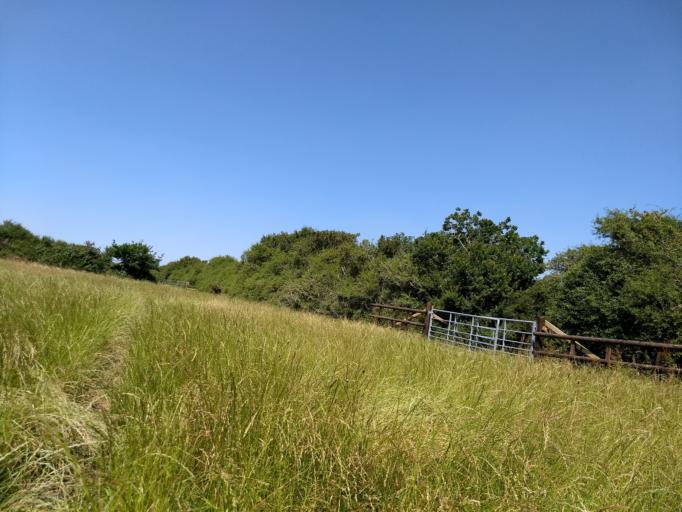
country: GB
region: England
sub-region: Isle of Wight
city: Gurnard
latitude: 50.7264
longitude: -1.3618
